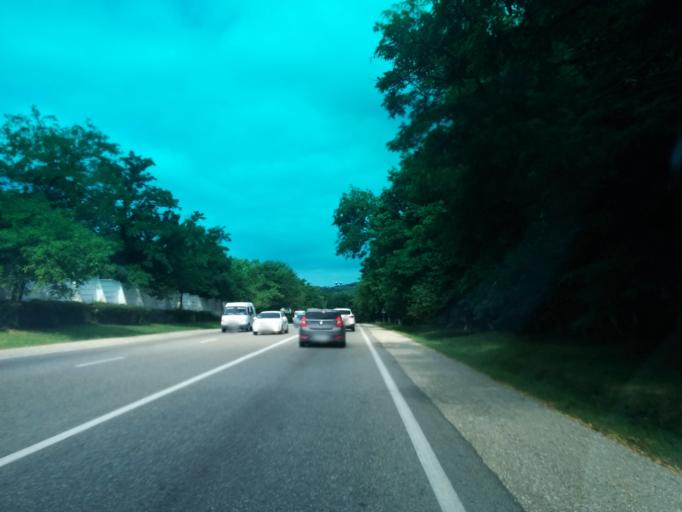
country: RU
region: Krasnodarskiy
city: Nebug
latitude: 44.1705
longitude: 38.9799
